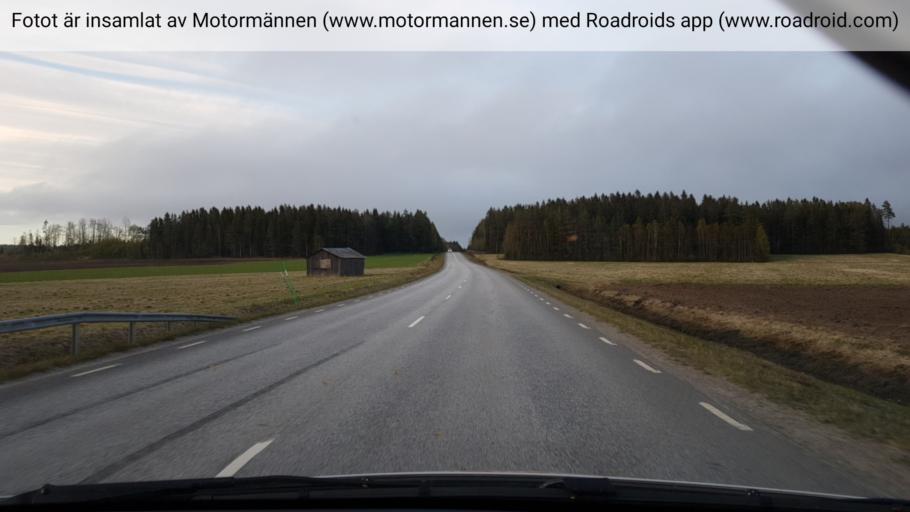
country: SE
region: Vaesterbotten
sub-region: Umea Kommun
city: Roback
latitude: 63.7776
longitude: 20.0673
